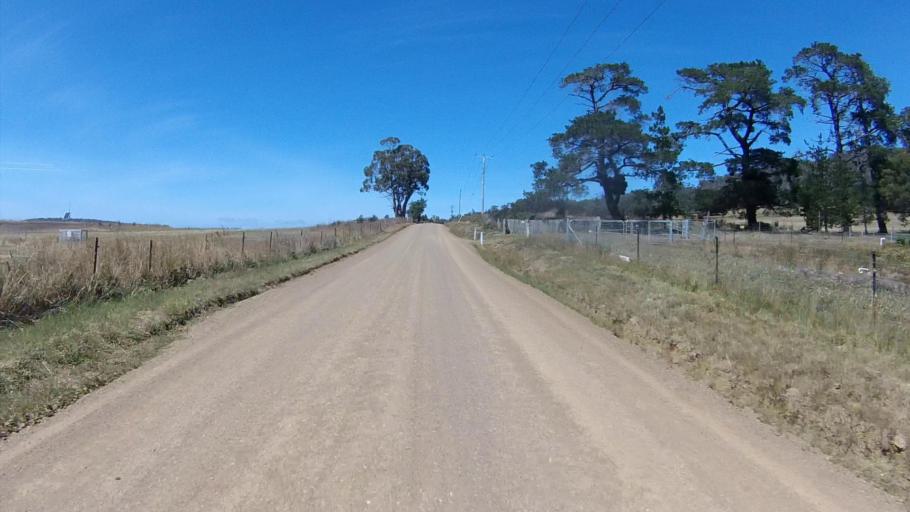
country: AU
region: Tasmania
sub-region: Sorell
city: Sorell
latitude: -42.7869
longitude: 147.6385
